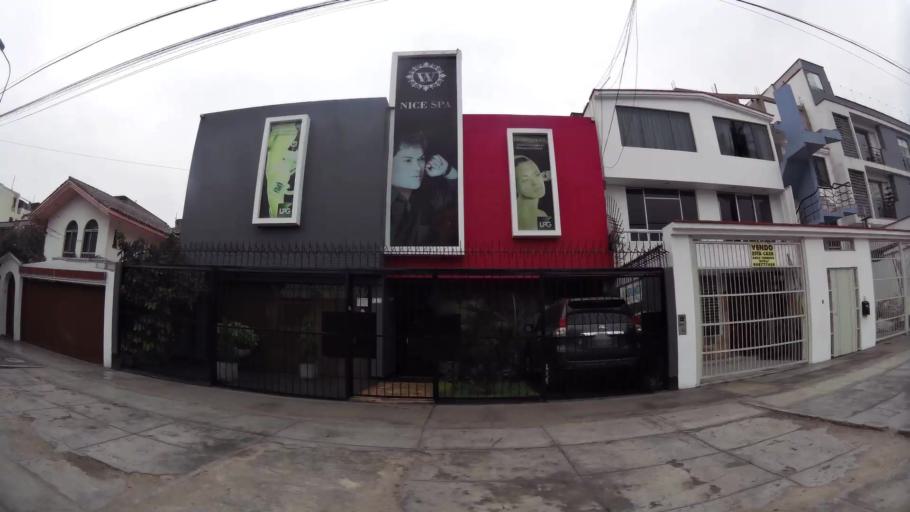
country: PE
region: Lima
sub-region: Lima
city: San Luis
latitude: -12.0905
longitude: -77.0007
